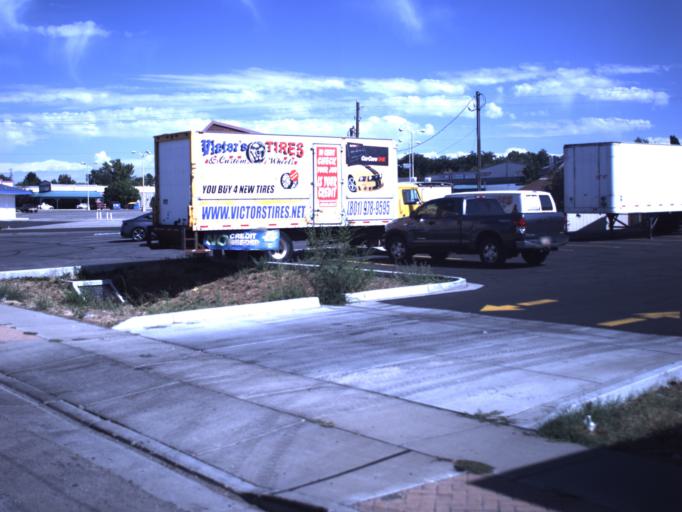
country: US
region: Utah
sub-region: Davis County
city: Clearfield
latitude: 41.1066
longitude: -112.0186
